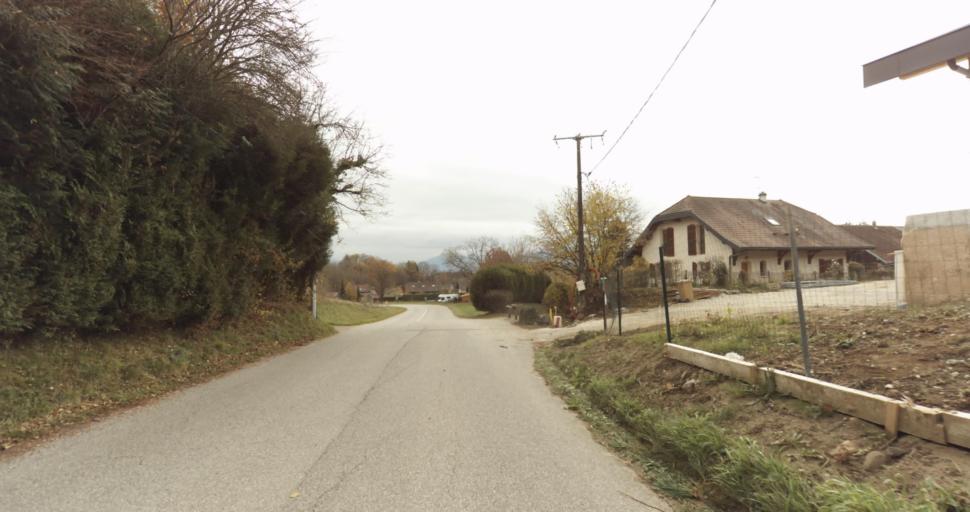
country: FR
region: Rhone-Alpes
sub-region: Departement de la Haute-Savoie
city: Pringy
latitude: 45.9567
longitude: 6.1082
